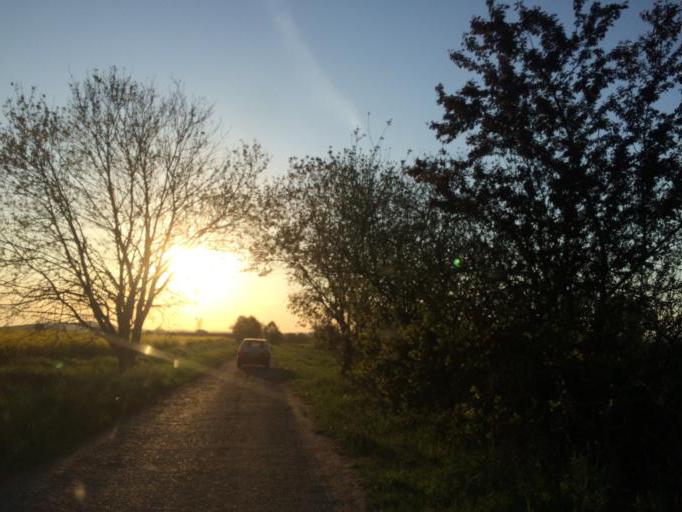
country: CZ
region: Central Bohemia
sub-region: Okres Mlada Boleslav
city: Zd'ar
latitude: 50.5415
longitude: 15.0618
